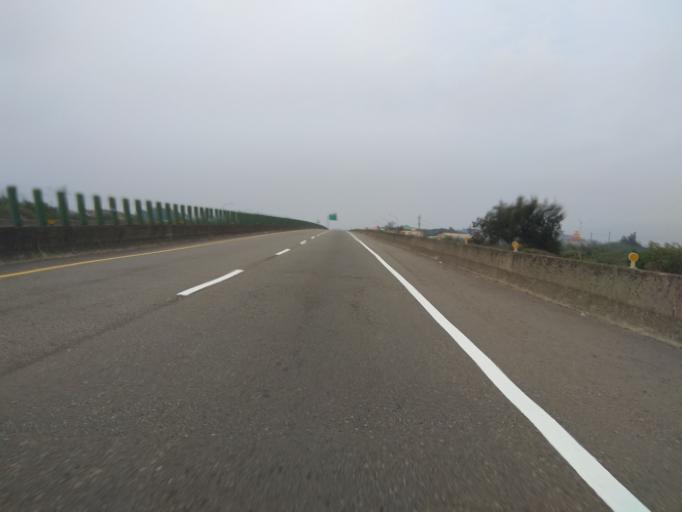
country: TW
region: Taiwan
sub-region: Miaoli
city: Miaoli
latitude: 24.6615
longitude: 120.8169
